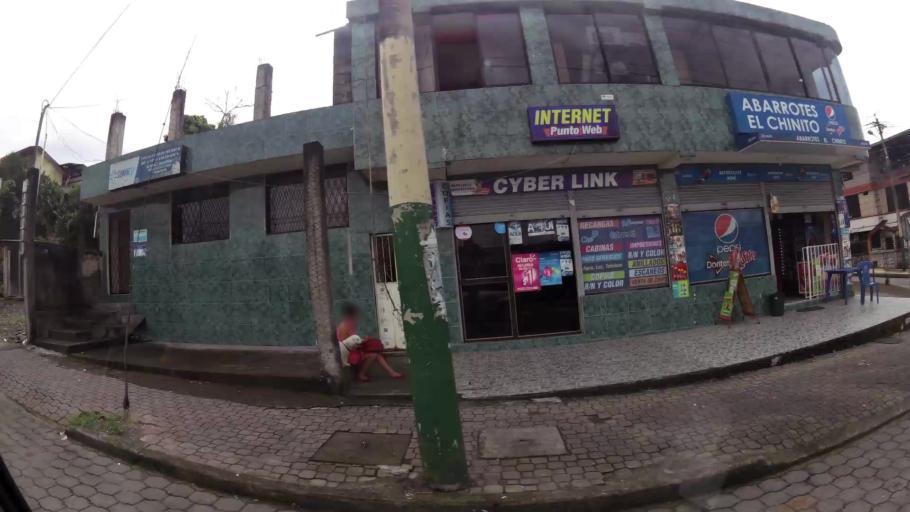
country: EC
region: Pastaza
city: Puyo
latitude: -1.4958
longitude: -78.0007
